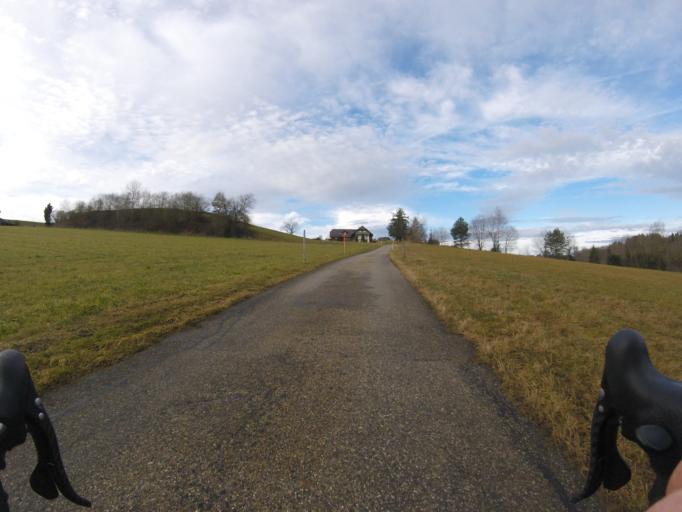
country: CH
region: Fribourg
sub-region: Sense District
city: Flamatt
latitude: 46.9142
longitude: 7.3551
